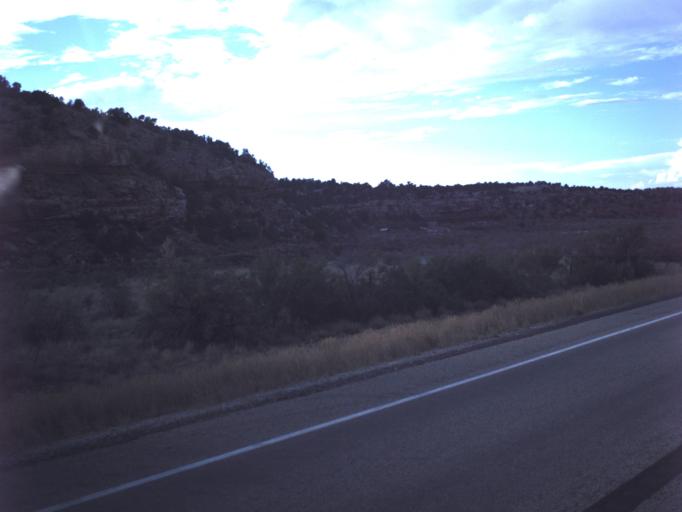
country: US
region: Utah
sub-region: San Juan County
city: Monticello
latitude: 38.0170
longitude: -109.3494
